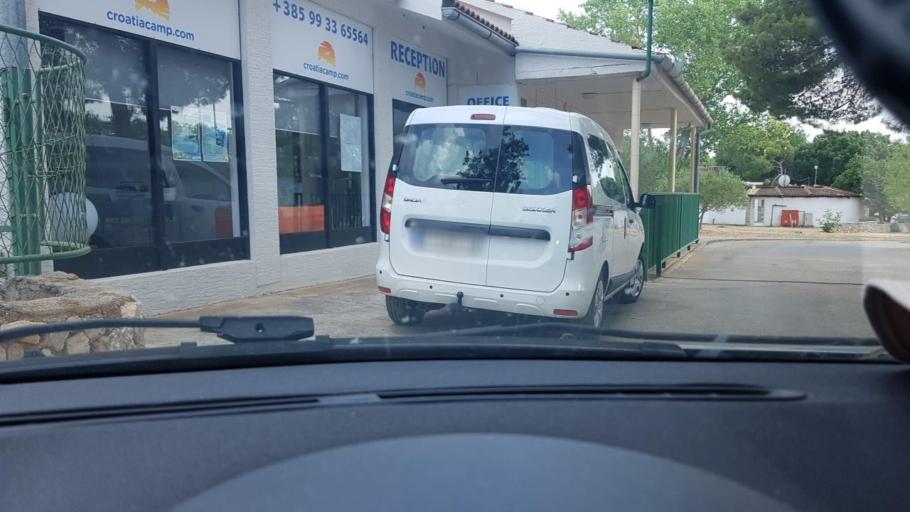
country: HR
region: Sibensko-Kniniska
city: Vodice
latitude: 43.7529
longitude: 15.7900
